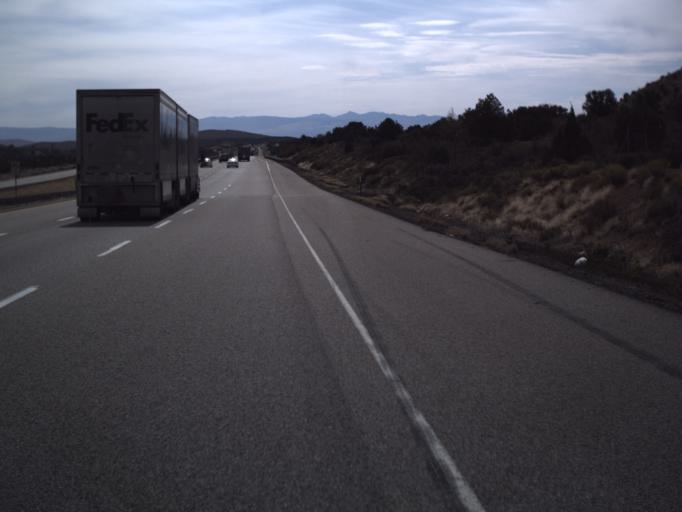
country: US
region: Utah
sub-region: Washington County
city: Toquerville
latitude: 37.2805
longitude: -113.3100
